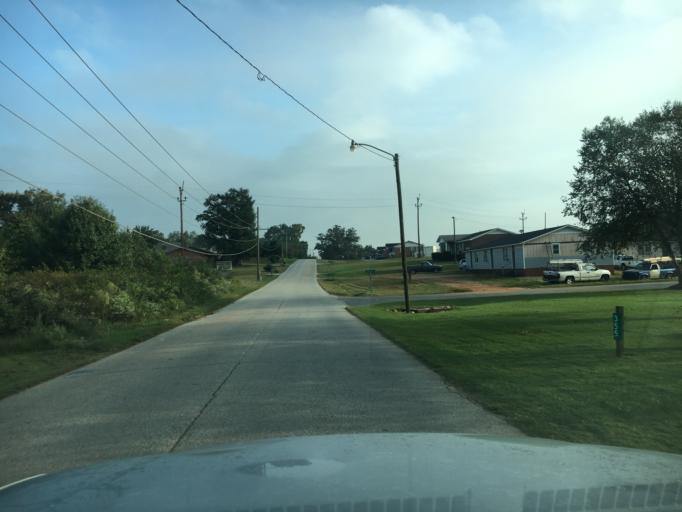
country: US
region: South Carolina
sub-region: Spartanburg County
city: Lyman
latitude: 34.9503
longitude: -82.1304
